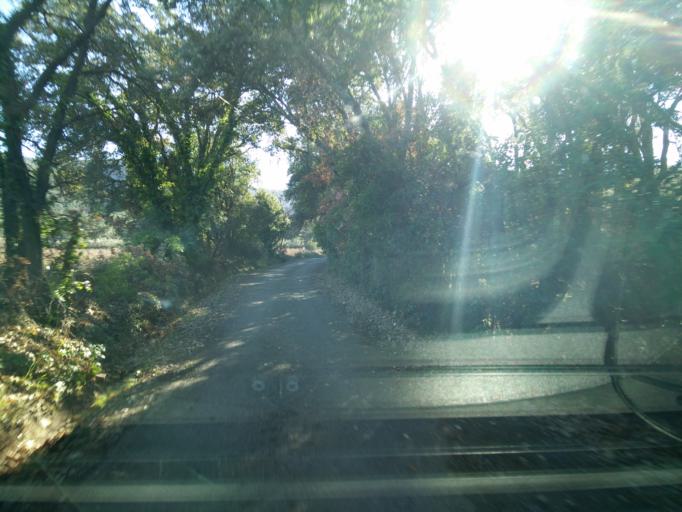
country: FR
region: Provence-Alpes-Cote d'Azur
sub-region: Departement du Var
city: Gonfaron
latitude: 43.3078
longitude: 6.2903
